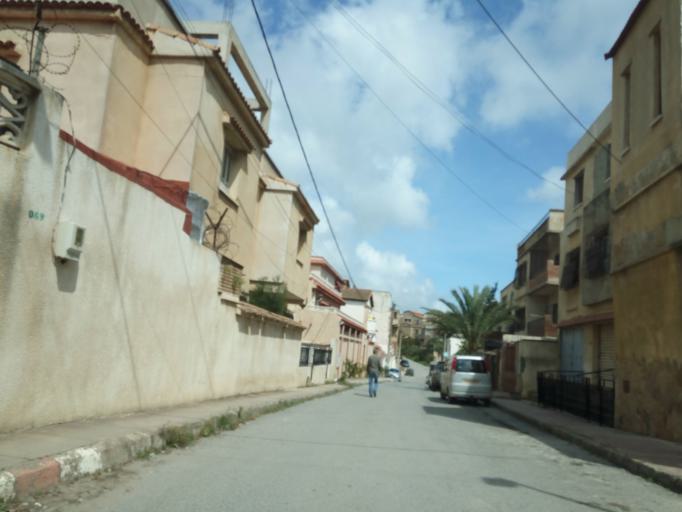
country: DZ
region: Tipaza
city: Douera
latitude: 36.7014
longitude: 2.9704
